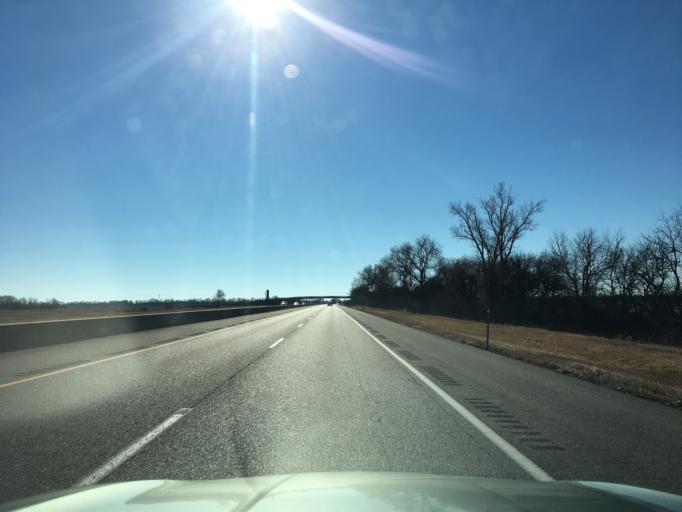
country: US
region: Kansas
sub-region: Sumner County
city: Belle Plaine
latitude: 37.4404
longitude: -97.3217
